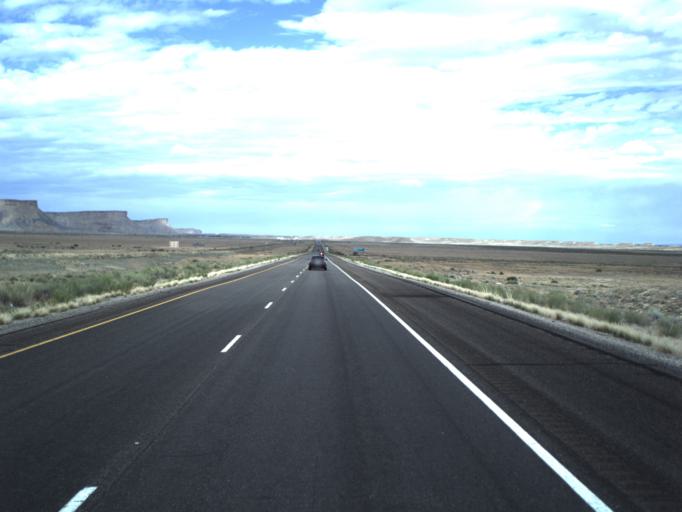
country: US
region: Utah
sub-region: Grand County
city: Moab
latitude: 38.9449
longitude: -109.7984
